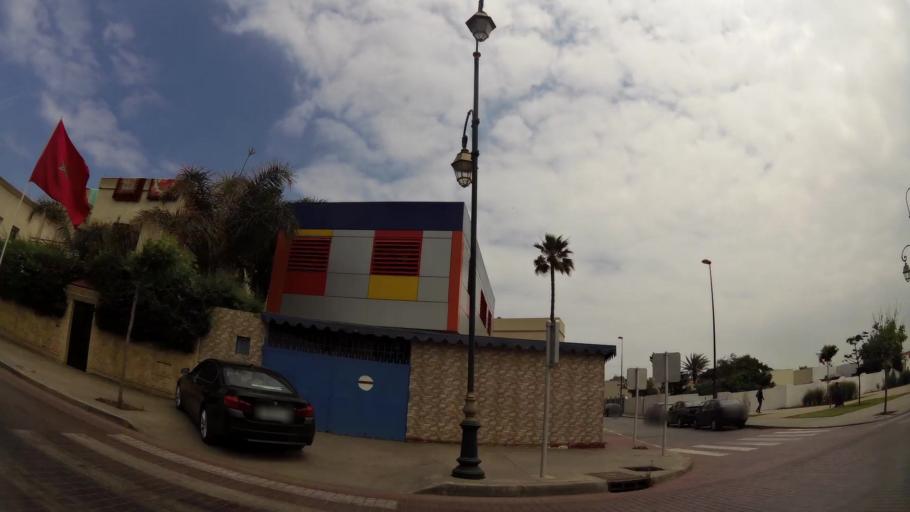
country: MA
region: Rabat-Sale-Zemmour-Zaer
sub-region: Skhirate-Temara
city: Temara
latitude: 33.9784
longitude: -6.8918
